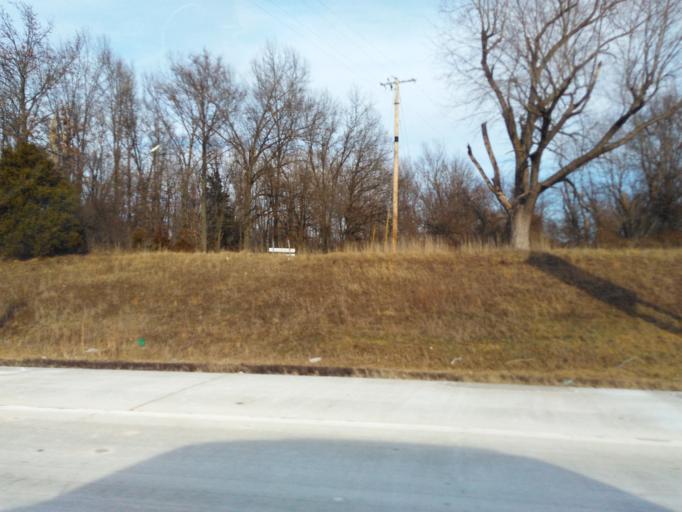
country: US
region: Illinois
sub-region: Jefferson County
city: Mount Vernon
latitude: 38.3050
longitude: -88.9484
